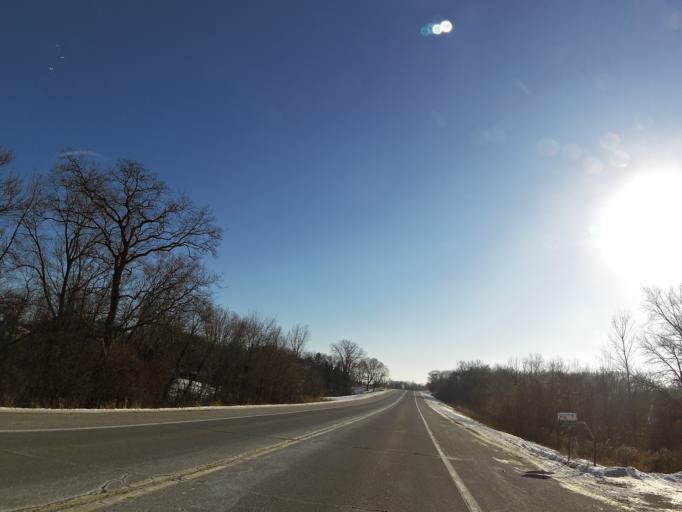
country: US
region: Minnesota
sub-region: Scott County
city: Prior Lake
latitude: 44.7093
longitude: -93.4904
